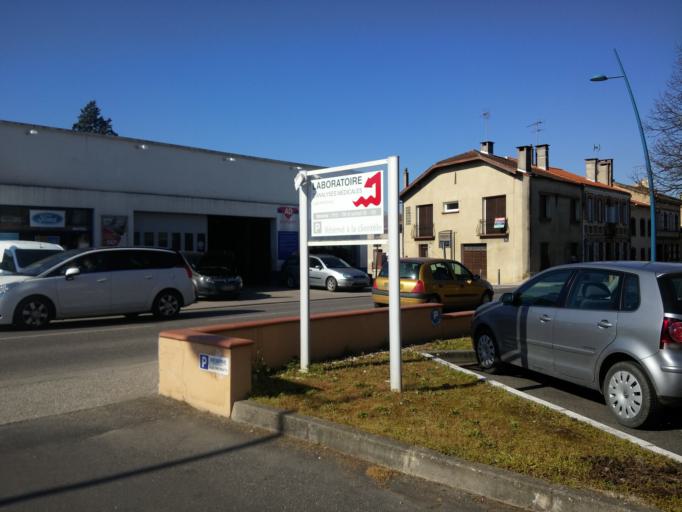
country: FR
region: Midi-Pyrenees
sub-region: Departement du Gers
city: Pujaudran
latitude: 43.6135
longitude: 1.0862
